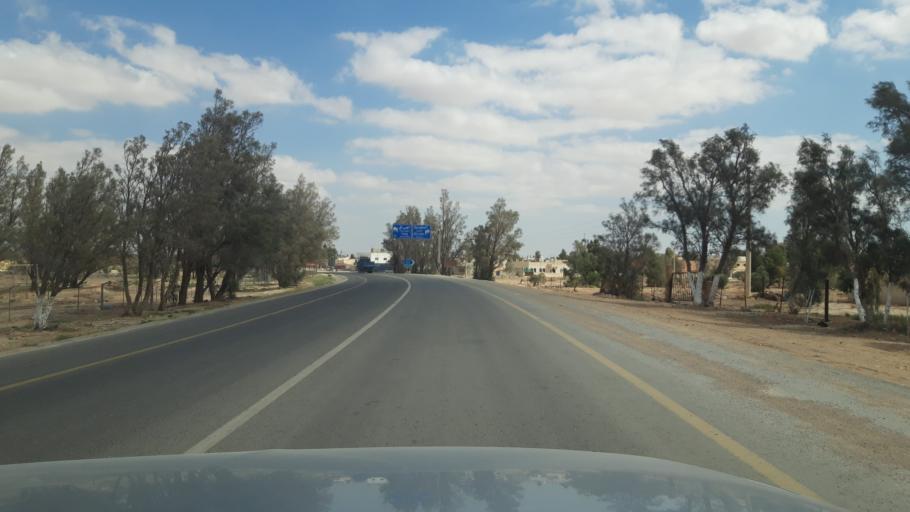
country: JO
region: Amman
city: Al Azraq ash Shamali
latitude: 31.8381
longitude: 36.8110
